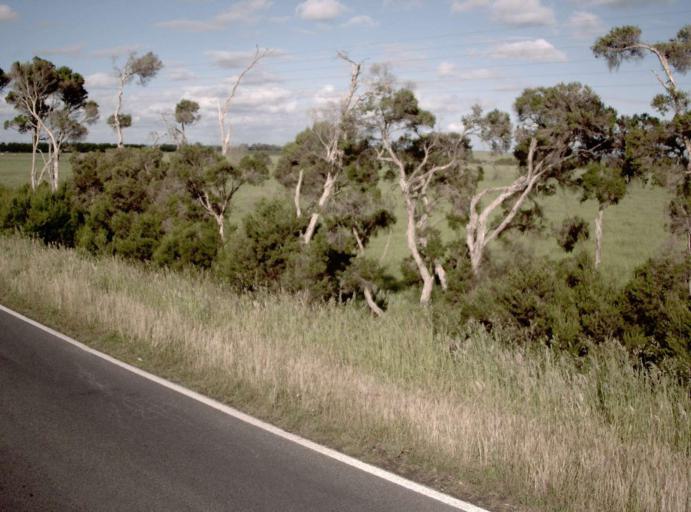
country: AU
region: Victoria
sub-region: Bass Coast
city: North Wonthaggi
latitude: -38.6216
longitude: 145.7359
